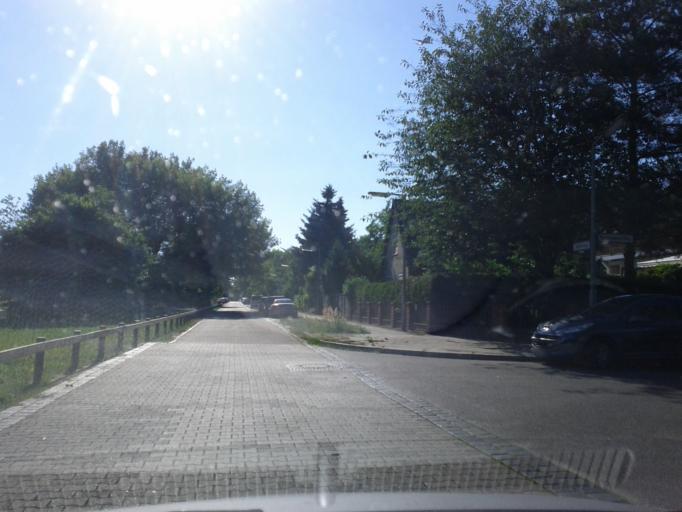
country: DE
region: Berlin
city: Falkenhagener Feld
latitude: 52.5440
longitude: 13.1731
